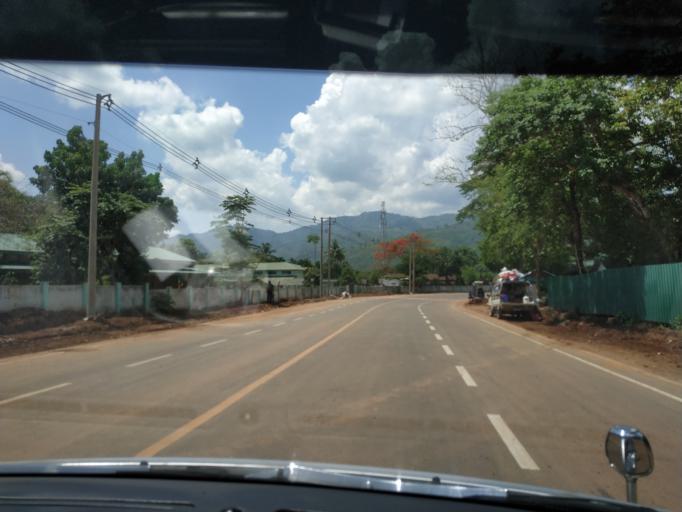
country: MM
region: Mon
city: Kyaikto
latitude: 17.3975
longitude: 97.0754
